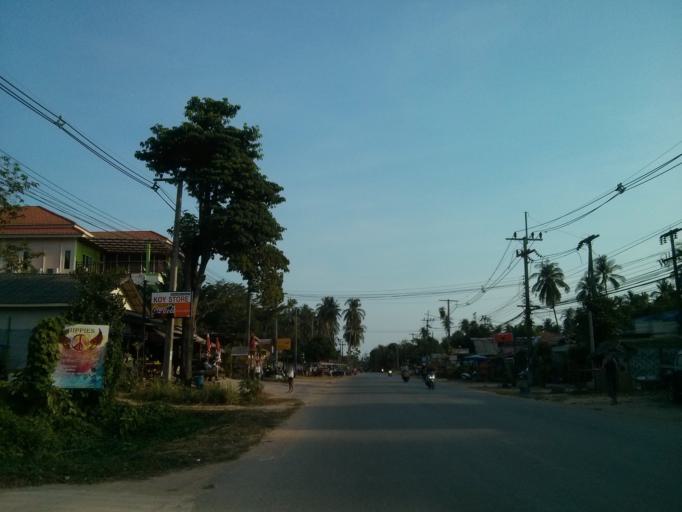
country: TH
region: Krabi
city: Saladan
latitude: 7.5761
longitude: 99.0349
